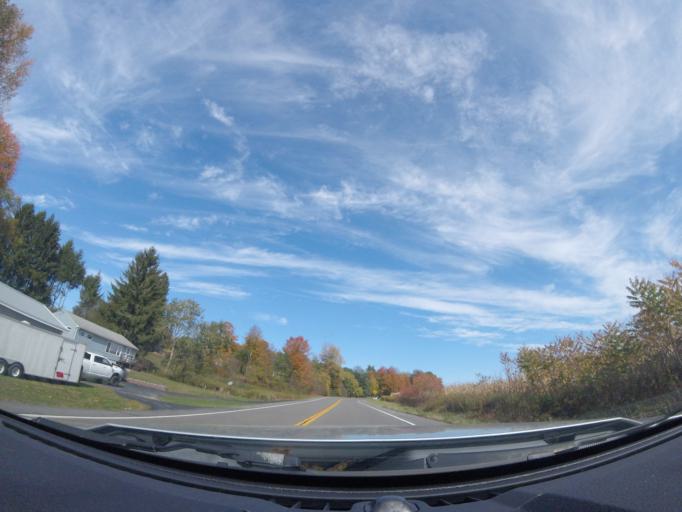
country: US
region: New York
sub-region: Cortland County
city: Cortland West
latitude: 42.5723
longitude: -76.2475
